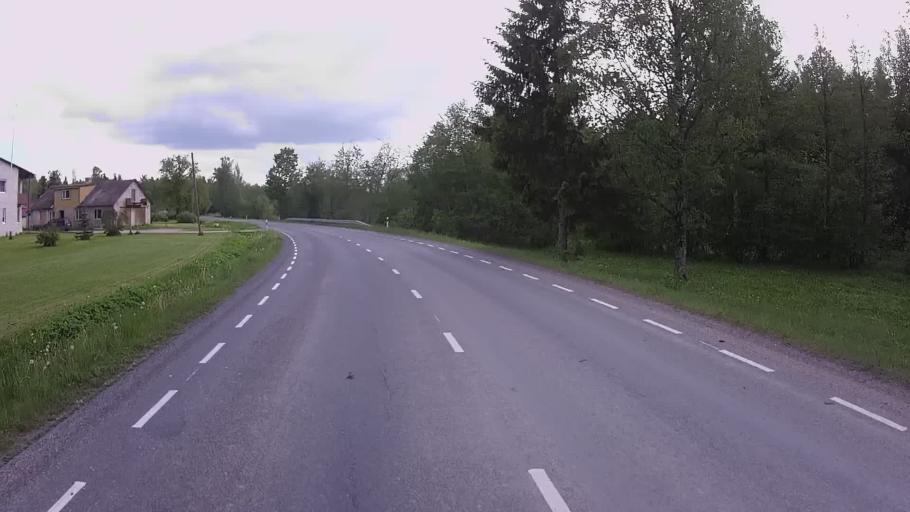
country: EE
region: Jogevamaa
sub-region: Mustvee linn
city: Mustvee
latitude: 58.9857
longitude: 26.8416
